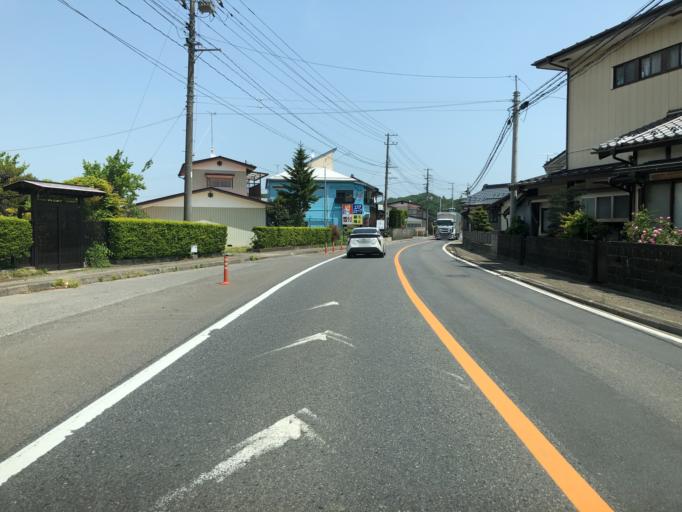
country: JP
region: Fukushima
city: Ishikawa
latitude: 37.1173
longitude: 140.2920
